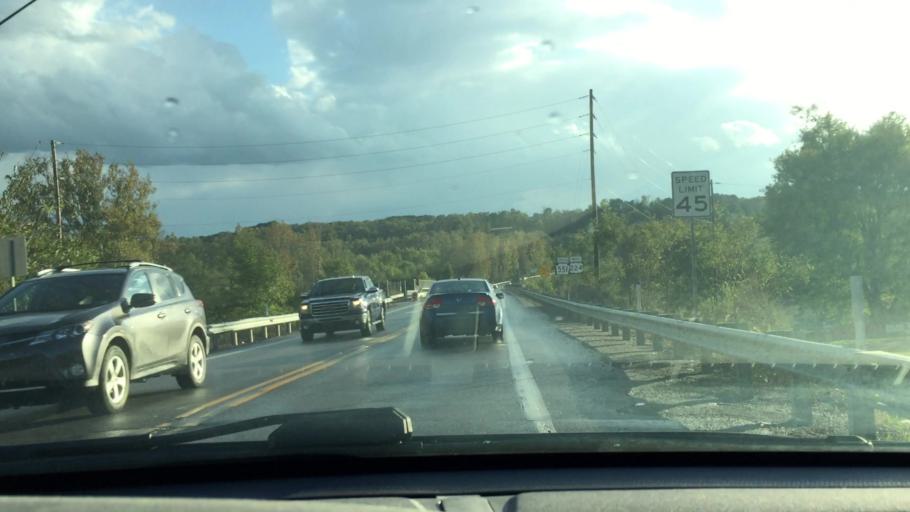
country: US
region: Pennsylvania
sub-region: Lawrence County
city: Oakwood
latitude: 41.0199
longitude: -80.4396
